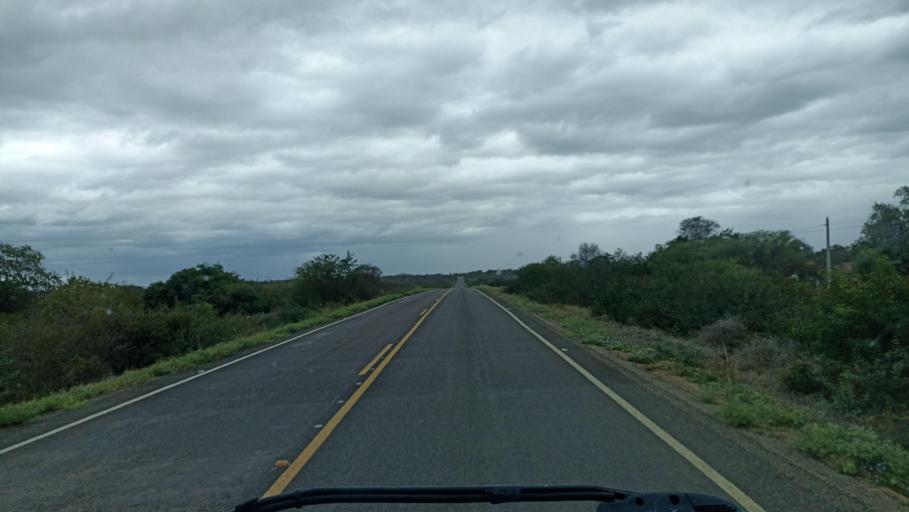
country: BR
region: Bahia
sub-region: Iacu
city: Iacu
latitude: -12.9722
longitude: -40.5036
